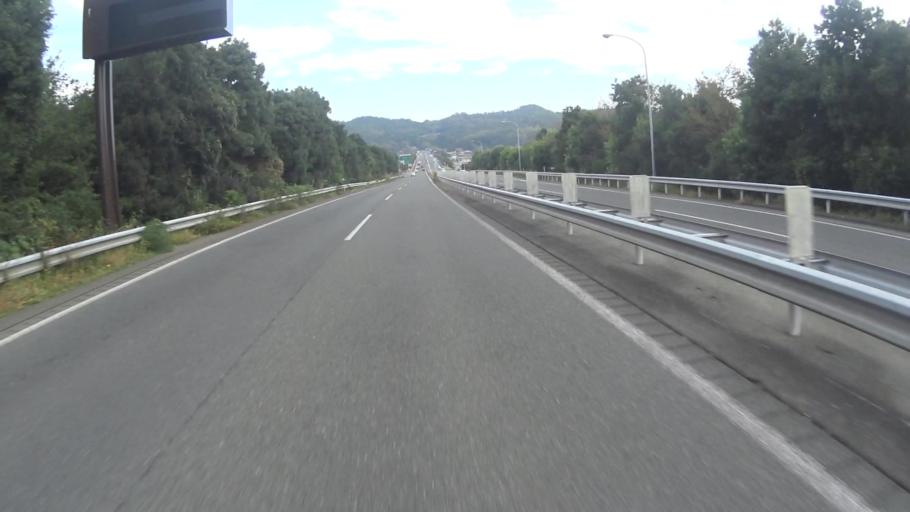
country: JP
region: Kyoto
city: Kameoka
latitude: 35.0458
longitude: 135.5345
